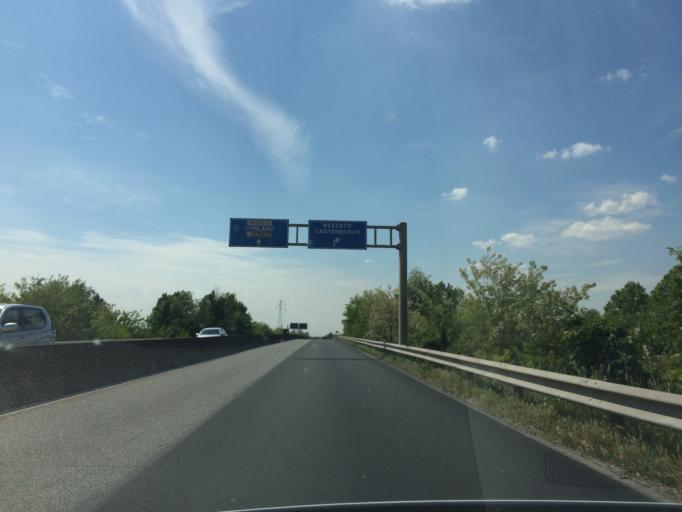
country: IT
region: Lombardy
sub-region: Provincia di Brescia
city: Rezzato
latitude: 45.4974
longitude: 10.3124
